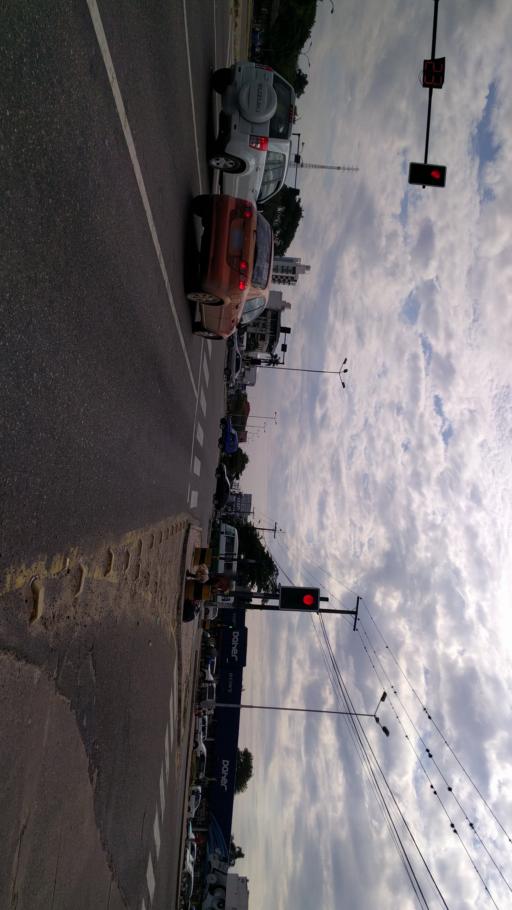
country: BO
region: Santa Cruz
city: Santa Cruz de la Sierra
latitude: -17.7953
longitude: -63.1663
